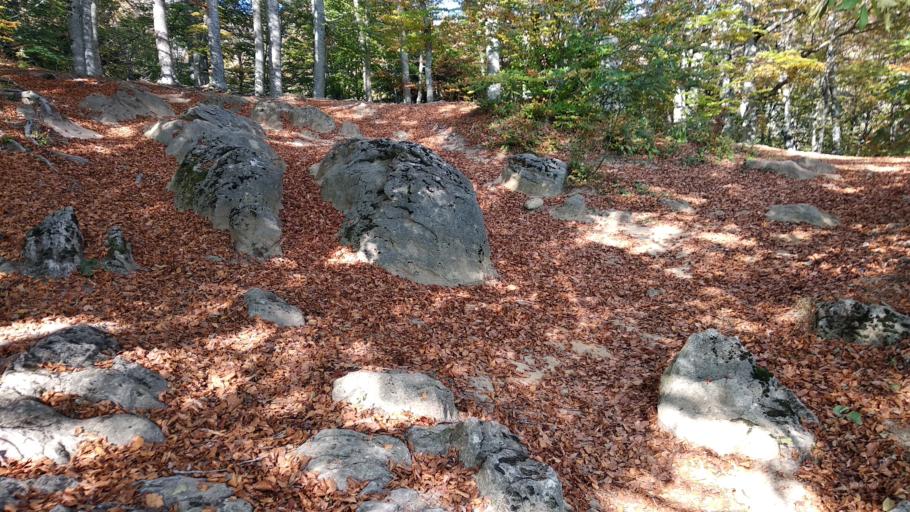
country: IT
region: Tuscany
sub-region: Province of Arezzo
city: Chiusi della Verna
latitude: 43.7076
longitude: 11.9305
